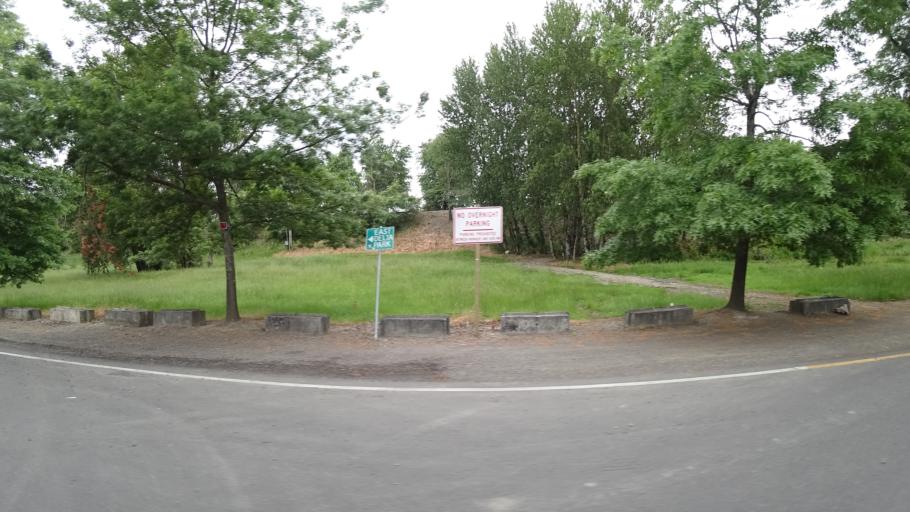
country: US
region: Washington
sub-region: Clark County
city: Vancouver
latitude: 45.5972
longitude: -122.6733
